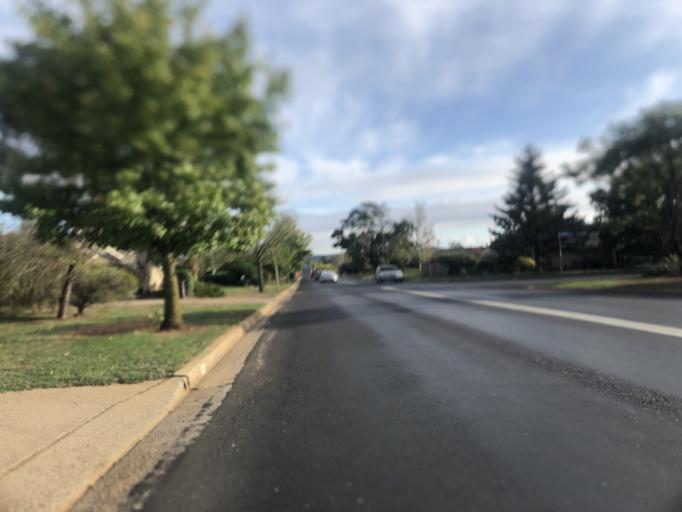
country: AU
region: New South Wales
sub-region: Orange Municipality
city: Orange
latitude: -33.3044
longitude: 149.0946
